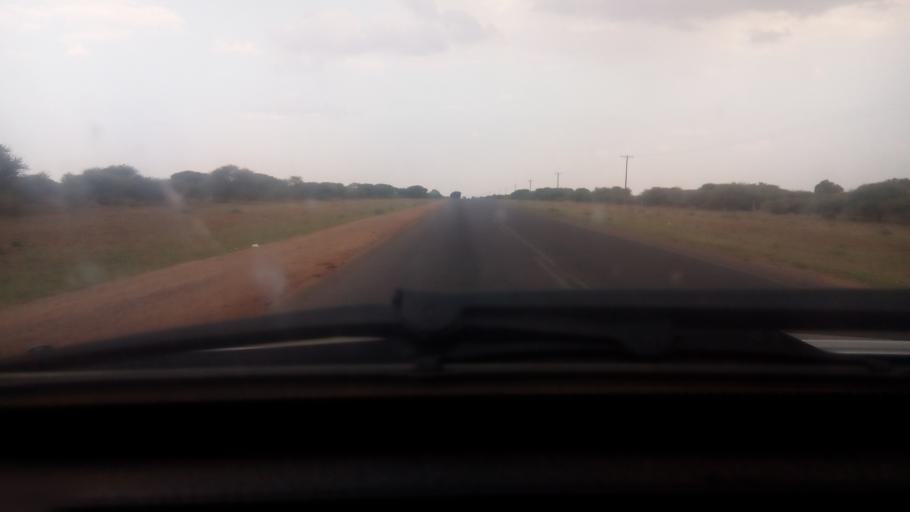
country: BW
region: Kweneng
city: Metsemotlhaba
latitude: -24.4718
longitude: 25.6981
